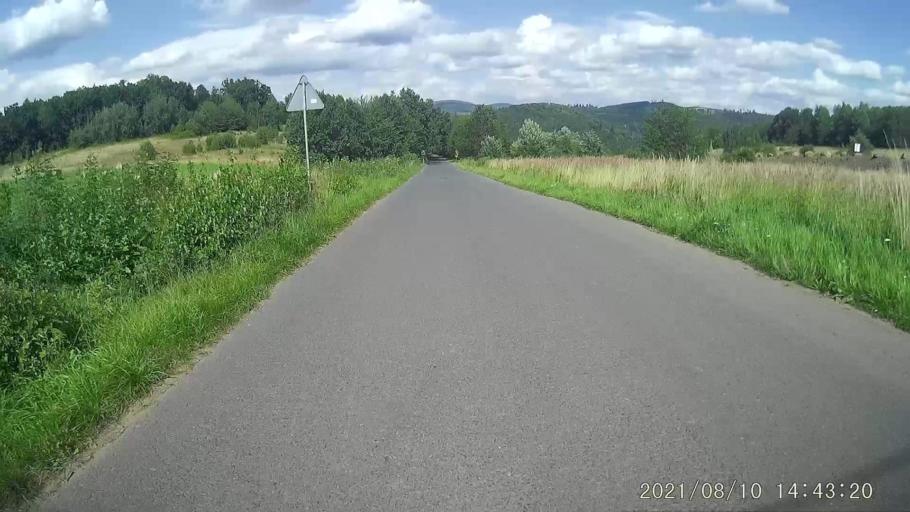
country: PL
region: Lower Silesian Voivodeship
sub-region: Powiat klodzki
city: Radkow
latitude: 50.5474
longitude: 16.4295
